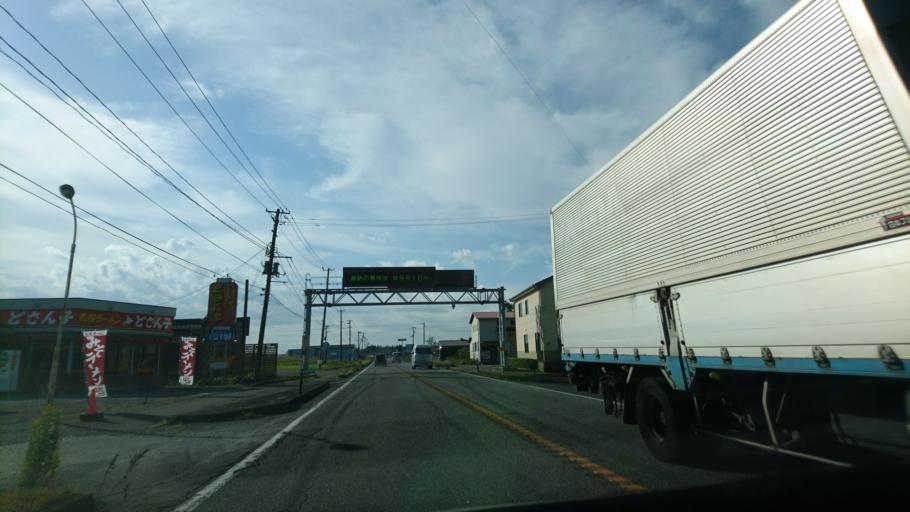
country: JP
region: Miyagi
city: Furukawa
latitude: 38.6130
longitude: 140.9834
